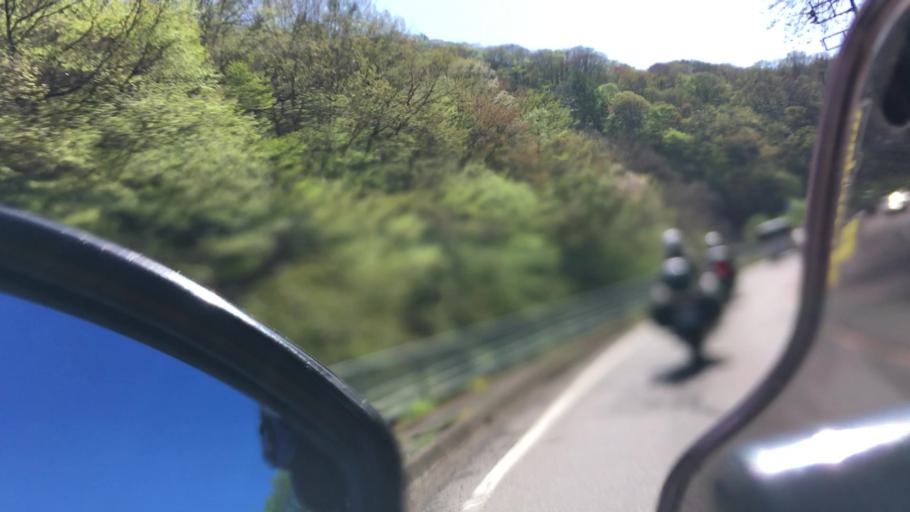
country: JP
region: Nagano
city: Komoro
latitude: 36.4852
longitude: 138.4765
